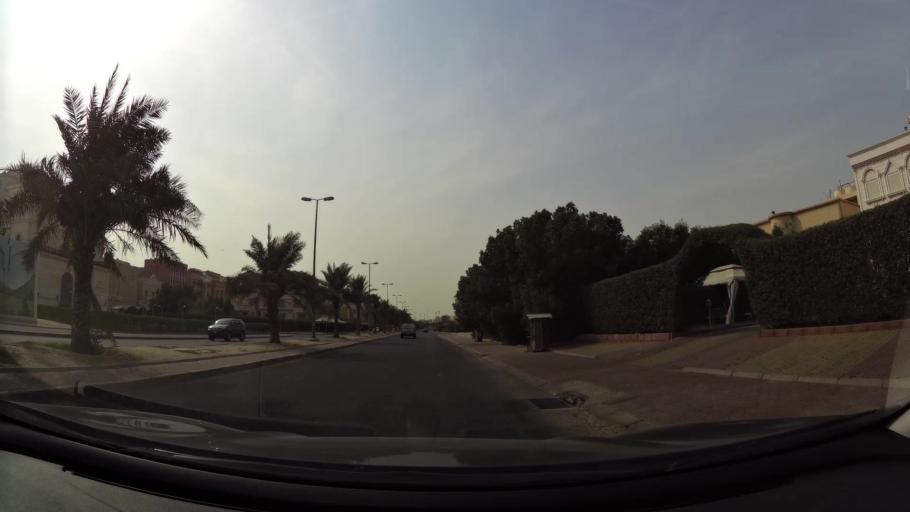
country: KW
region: Al Farwaniyah
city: Al Farwaniyah
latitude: 29.2687
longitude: 47.9390
